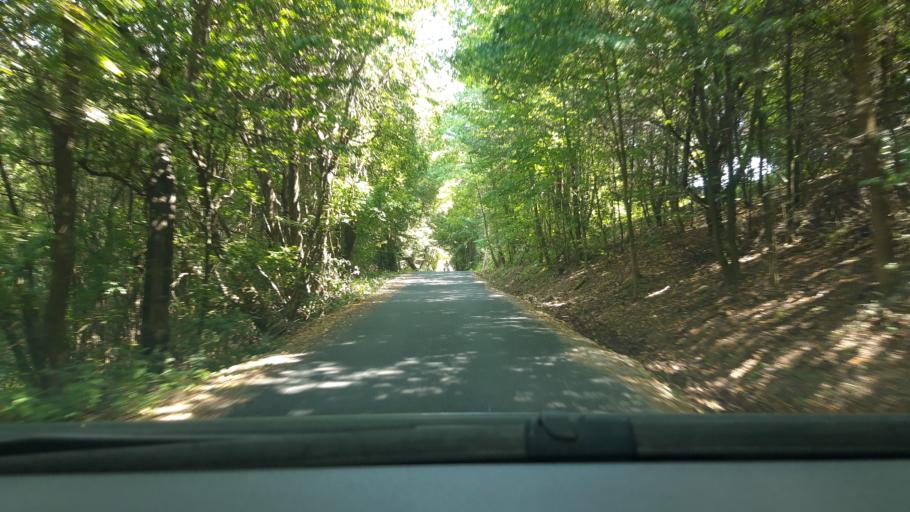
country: HU
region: Nograd
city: Somoskoujfalu
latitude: 48.1806
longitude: 19.8516
